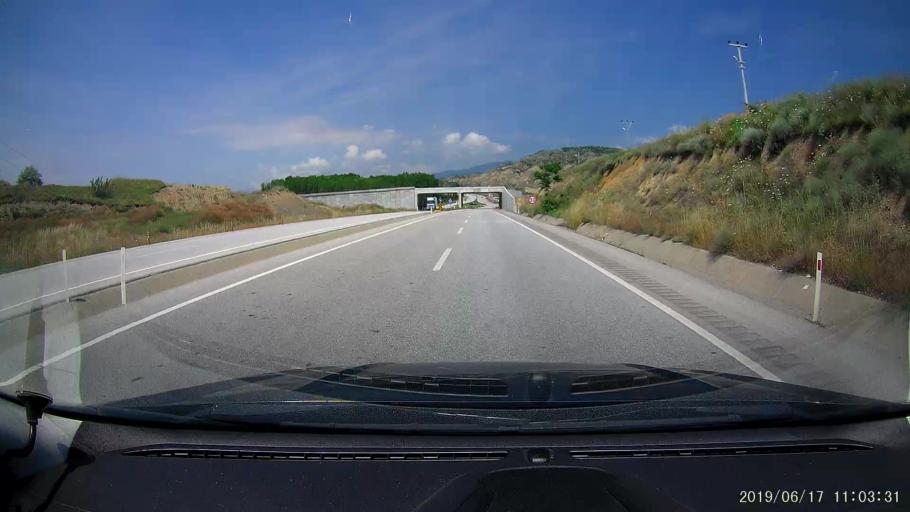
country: TR
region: Kastamonu
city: Tosya
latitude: 41.0180
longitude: 34.1143
